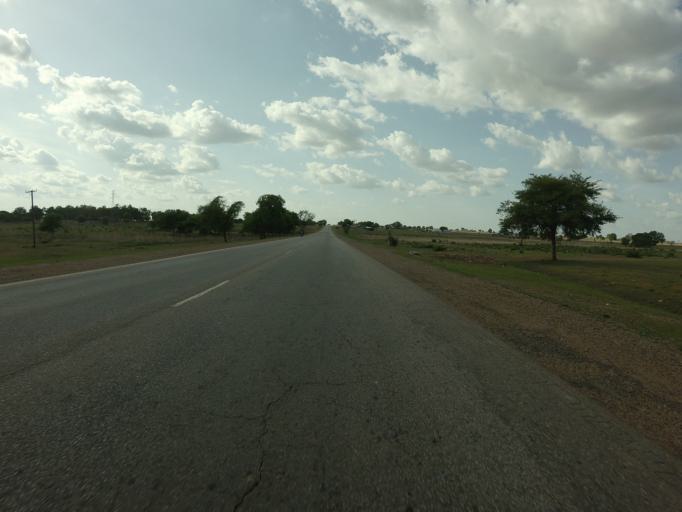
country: GH
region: Upper East
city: Bolgatanga
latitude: 10.6711
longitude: -0.8608
